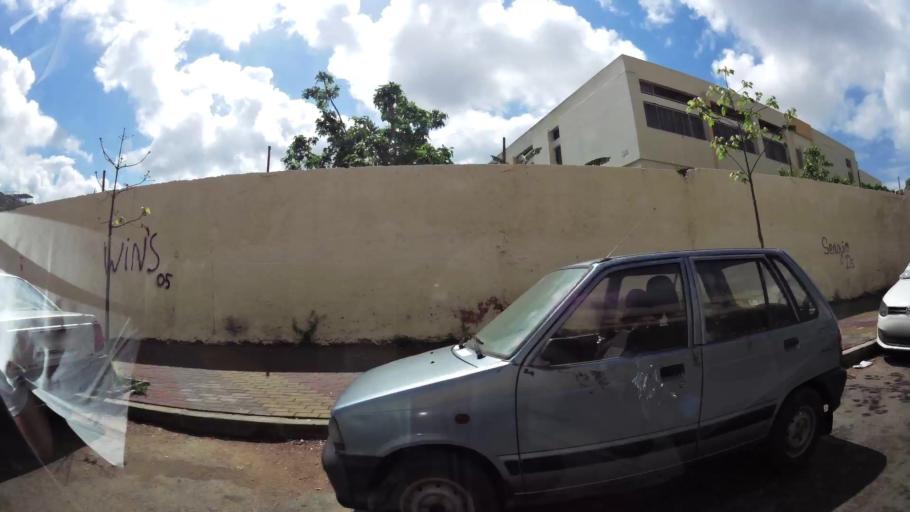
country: MA
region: Grand Casablanca
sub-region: Casablanca
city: Casablanca
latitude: 33.5604
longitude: -7.6050
